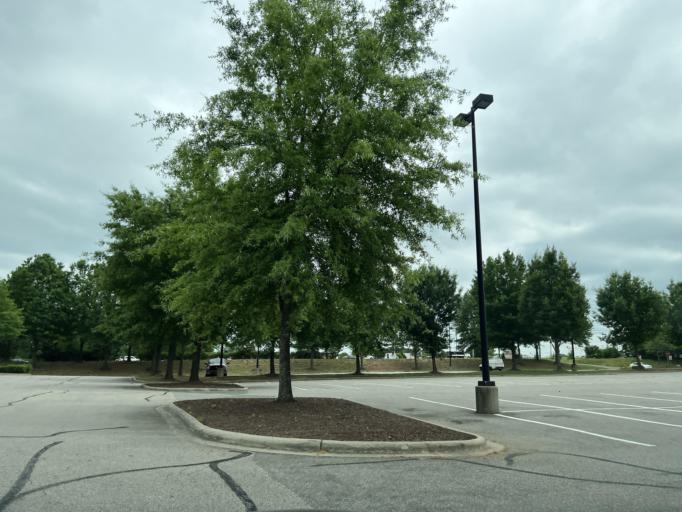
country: US
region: North Carolina
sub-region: Wake County
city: Raleigh
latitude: 35.8733
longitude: -78.5806
